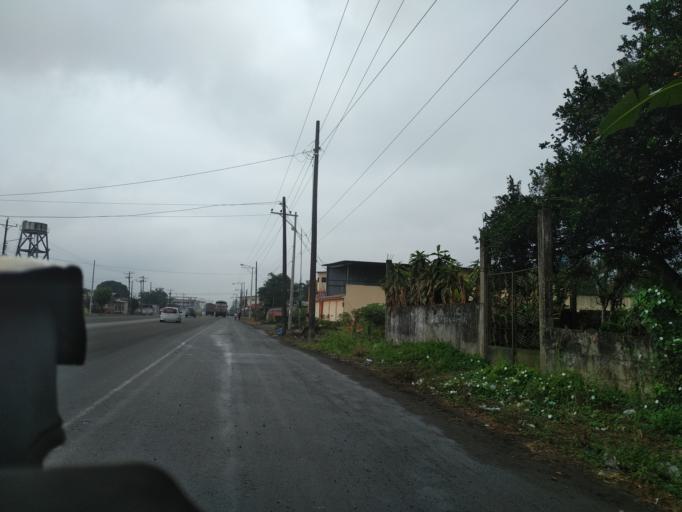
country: EC
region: Cotopaxi
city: La Mana
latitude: -0.9496
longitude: -79.3443
